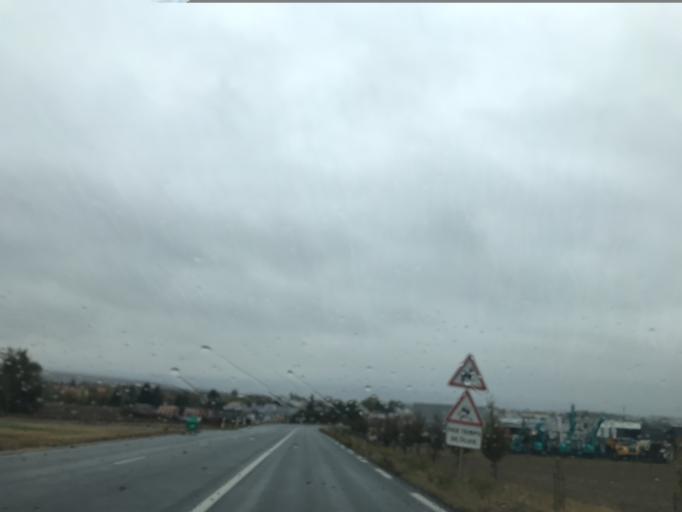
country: FR
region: Auvergne
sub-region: Departement du Puy-de-Dome
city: Dallet
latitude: 45.7732
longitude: 3.2129
